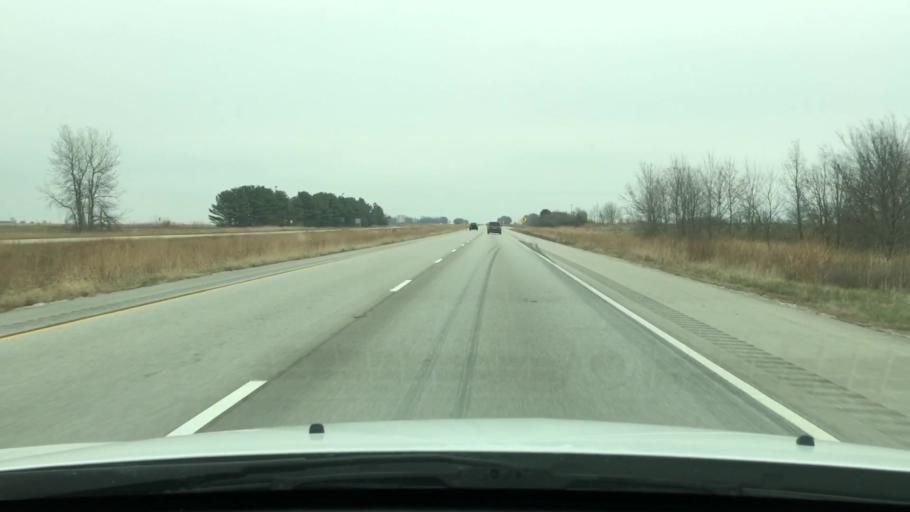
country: US
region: Illinois
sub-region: Sangamon County
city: New Berlin
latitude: 39.7368
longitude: -90.0409
